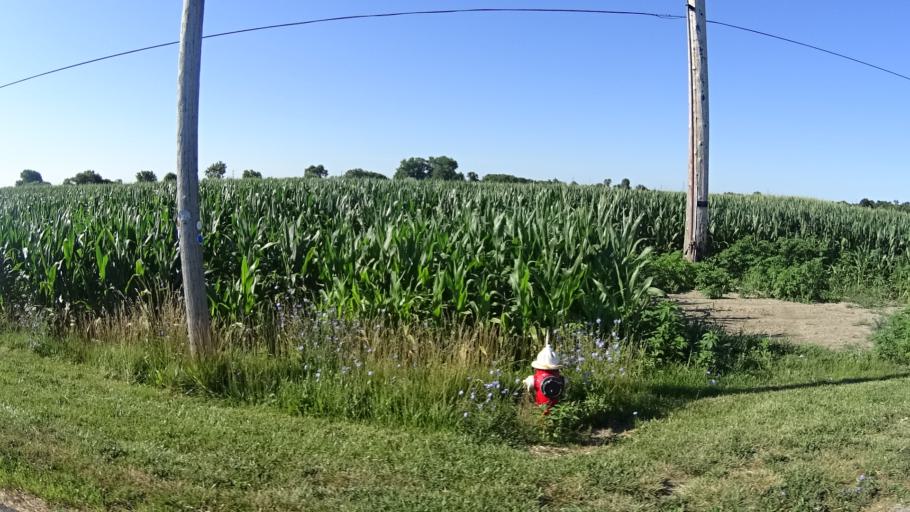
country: US
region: Ohio
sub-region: Erie County
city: Sandusky
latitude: 41.3974
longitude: -82.7508
